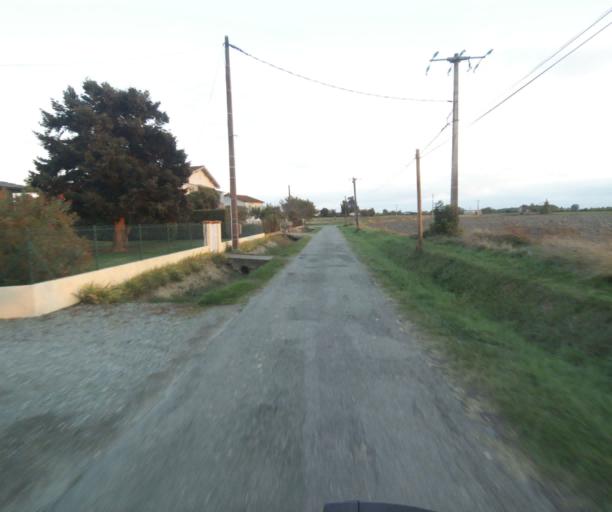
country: FR
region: Midi-Pyrenees
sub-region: Departement du Tarn-et-Garonne
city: Verdun-sur-Garonne
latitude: 43.8398
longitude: 1.2430
